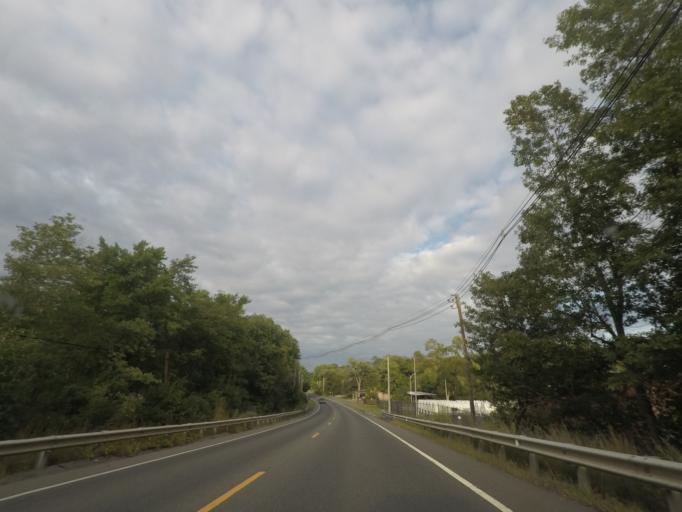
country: US
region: Massachusetts
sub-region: Hampshire County
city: Ware
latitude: 42.2100
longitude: -72.2481
